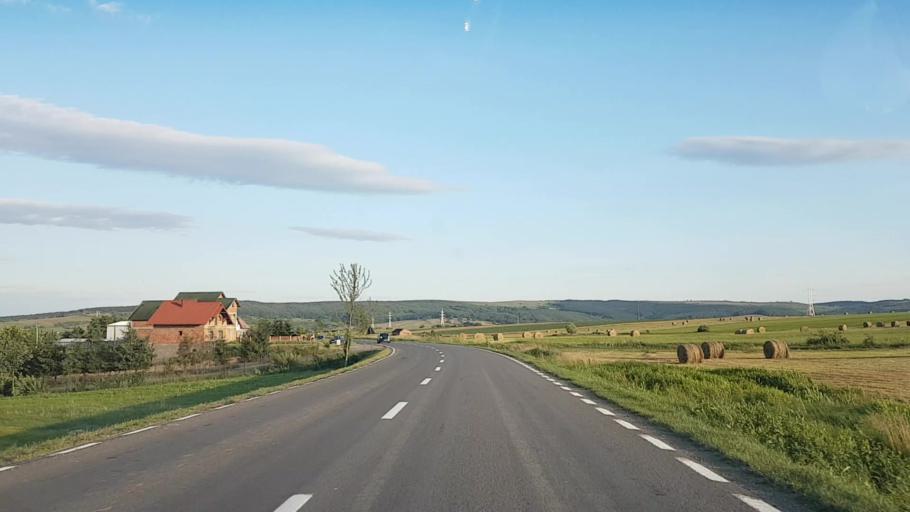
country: RO
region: Harghita
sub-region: Comuna Lupeni
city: Lupeni
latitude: 46.3754
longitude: 25.2199
